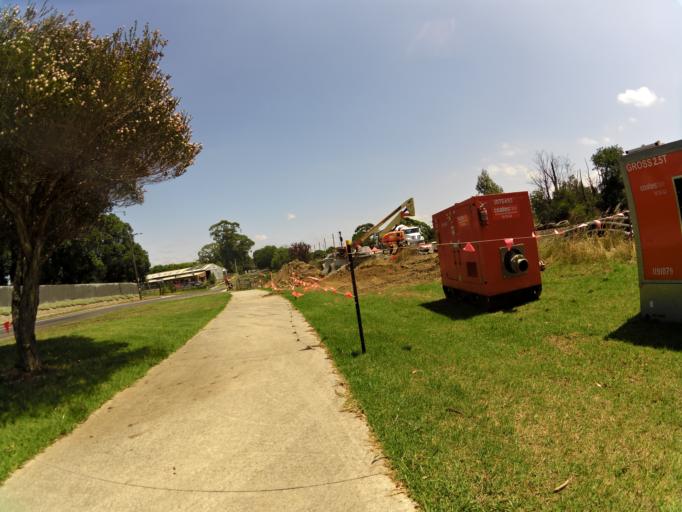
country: AU
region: Victoria
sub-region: Latrobe
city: Traralgon
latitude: -38.1969
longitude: 146.5466
